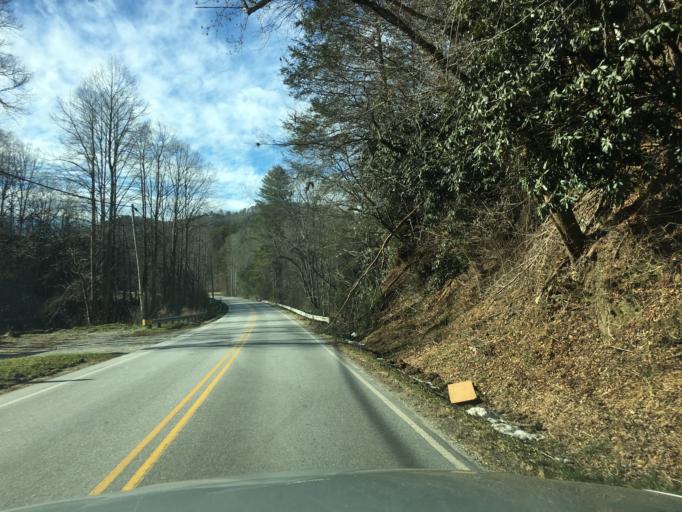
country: US
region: North Carolina
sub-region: Transylvania County
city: Brevard
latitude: 35.1400
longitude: -82.8439
